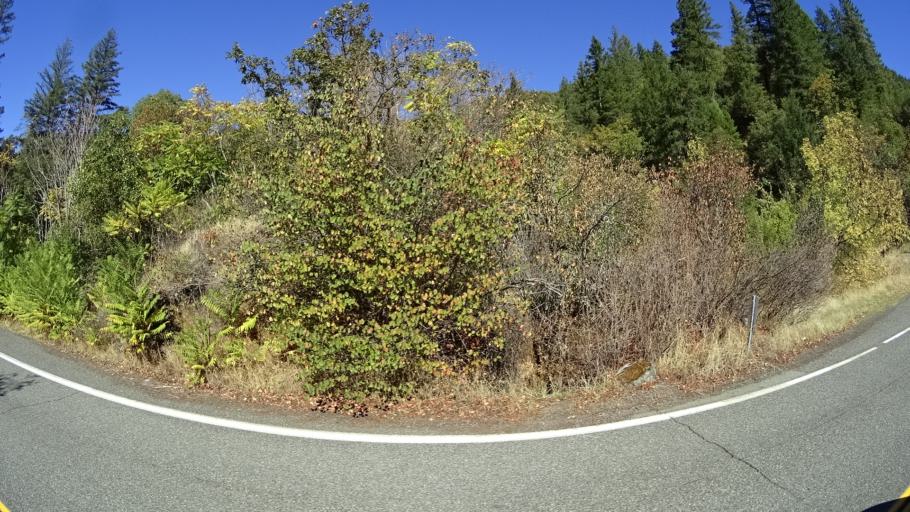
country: US
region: California
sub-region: Siskiyou County
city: Happy Camp
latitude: 41.3797
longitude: -123.4714
